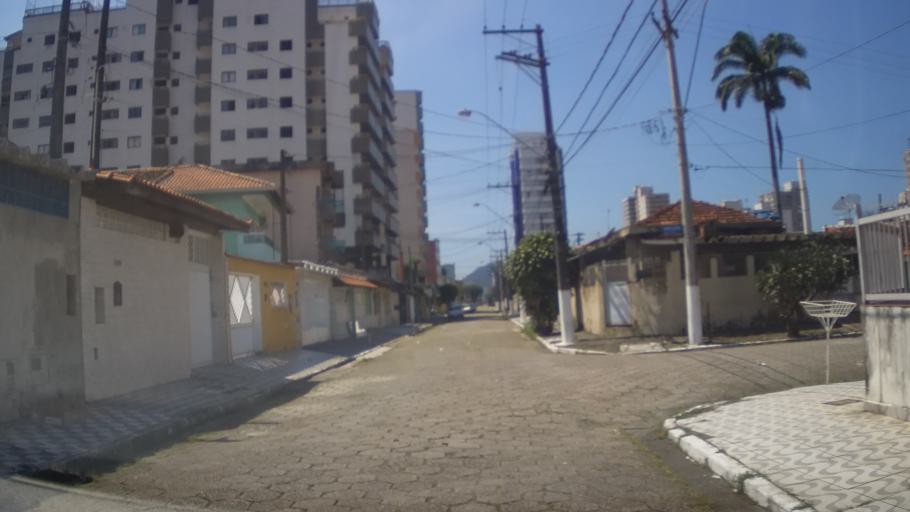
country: BR
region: Sao Paulo
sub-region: Praia Grande
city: Praia Grande
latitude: -24.0171
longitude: -46.4501
